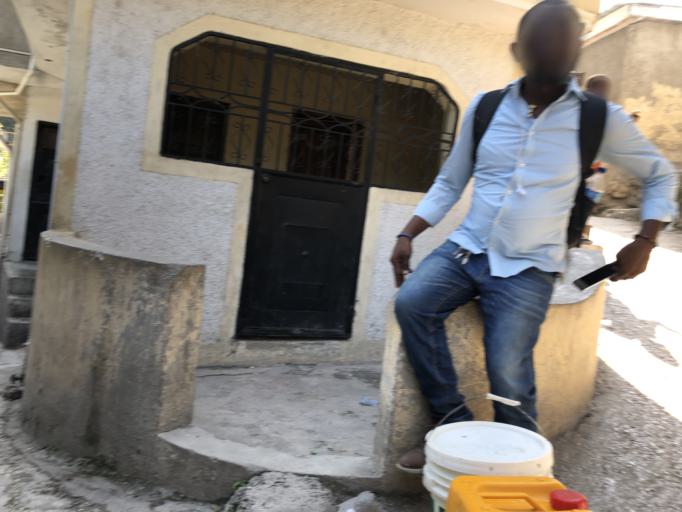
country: HT
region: Ouest
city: Port-au-Prince
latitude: 18.5247
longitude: -72.3179
